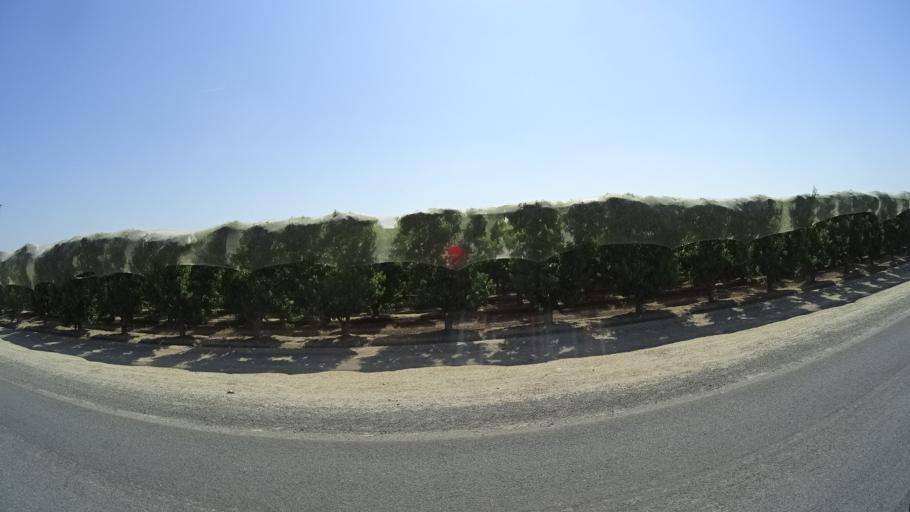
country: US
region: California
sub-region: Fresno County
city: Kingsburg
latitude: 36.4467
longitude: -119.5286
